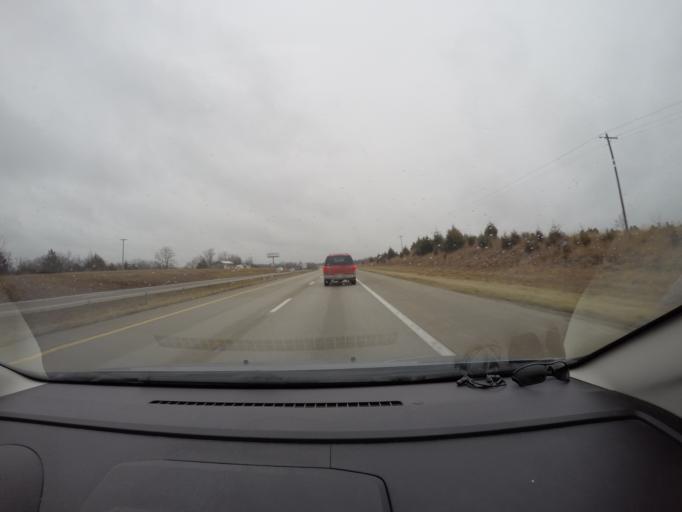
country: US
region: Missouri
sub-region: Callaway County
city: Fulton
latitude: 38.9290
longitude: -91.7887
